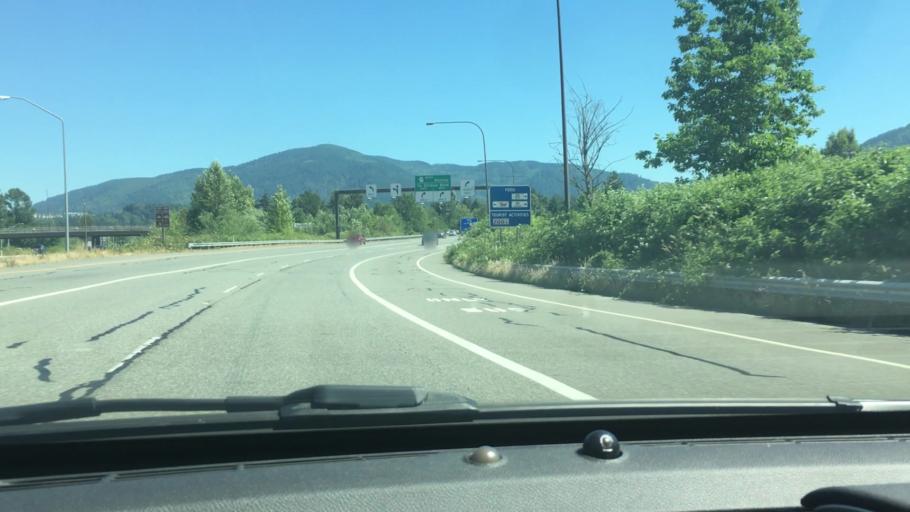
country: US
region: Washington
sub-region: King County
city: Issaquah
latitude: 47.5497
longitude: -122.0652
